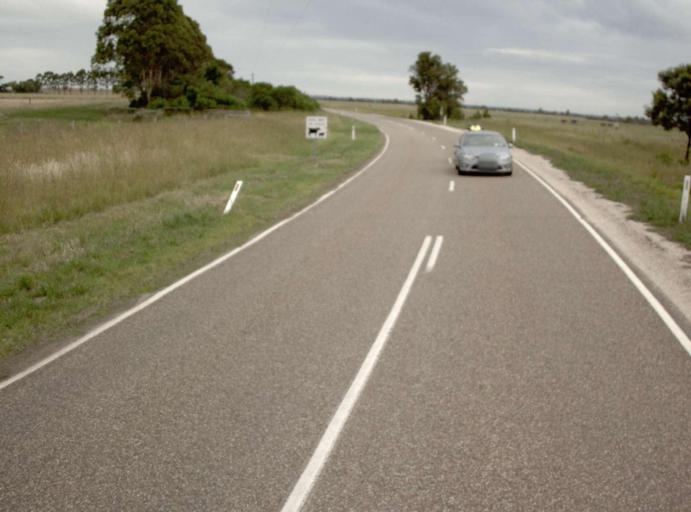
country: AU
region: Victoria
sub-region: Wellington
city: Sale
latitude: -38.0498
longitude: 147.1500
